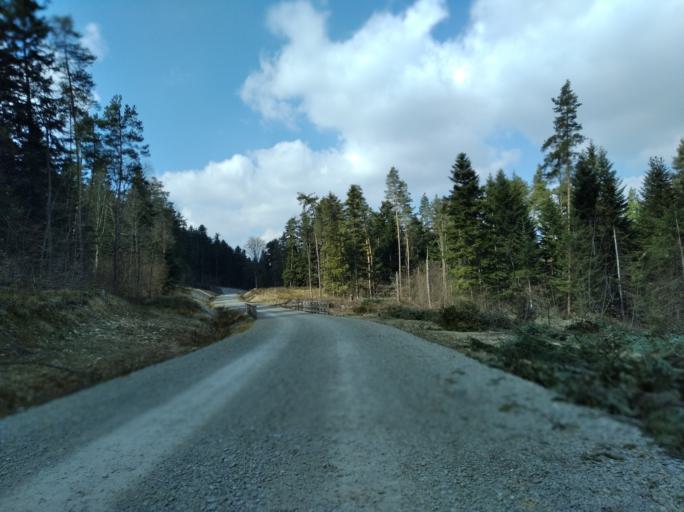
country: PL
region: Subcarpathian Voivodeship
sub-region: Powiat strzyzowski
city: Strzyzow
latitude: 49.8183
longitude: 21.8104
